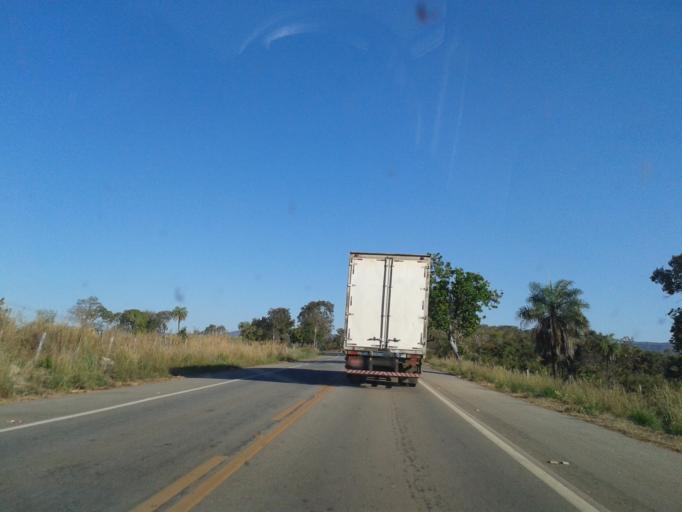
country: BR
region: Goias
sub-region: Itapuranga
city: Itapuranga
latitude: -15.4205
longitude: -50.3767
